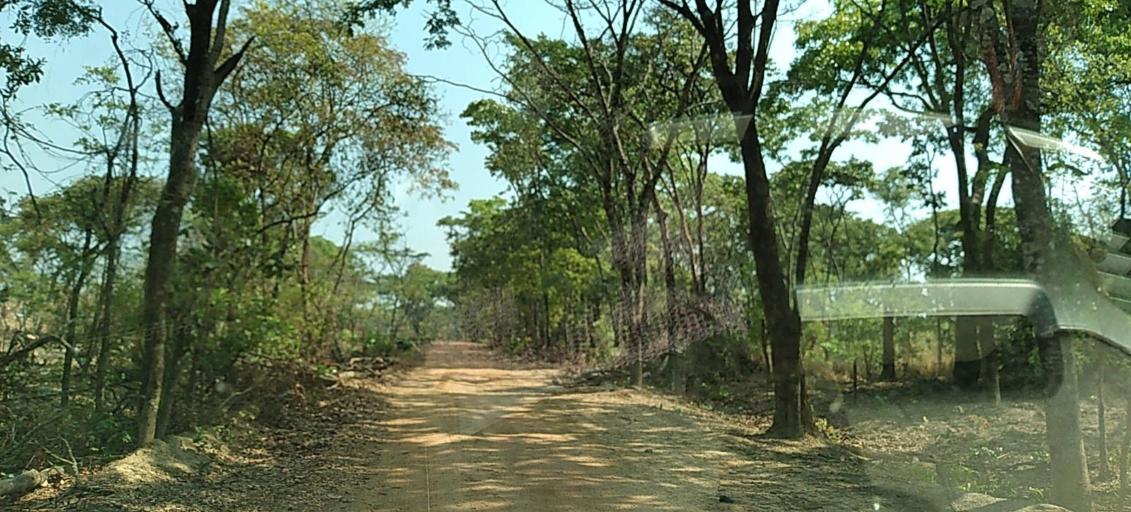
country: ZM
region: Copperbelt
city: Kalulushi
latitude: -12.9261
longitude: 27.8220
